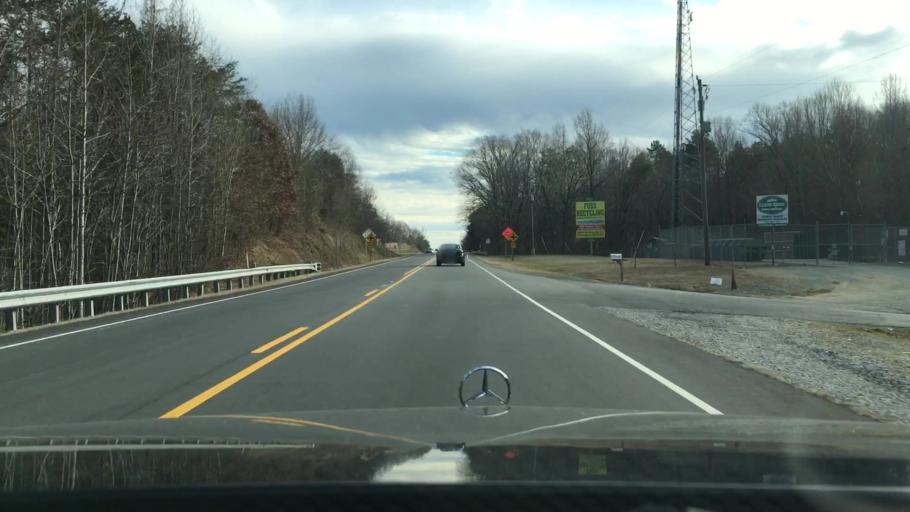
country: US
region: Virginia
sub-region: City of Danville
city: Danville
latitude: 36.4914
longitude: -79.3841
